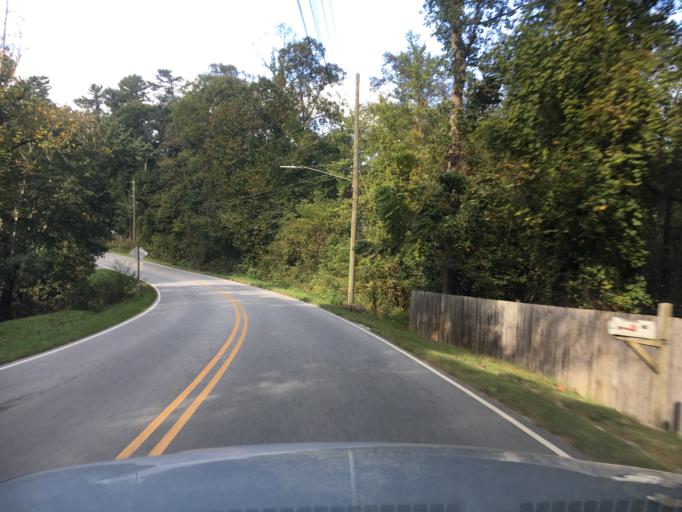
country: US
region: North Carolina
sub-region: Henderson County
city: Fletcher
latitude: 35.4360
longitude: -82.5173
